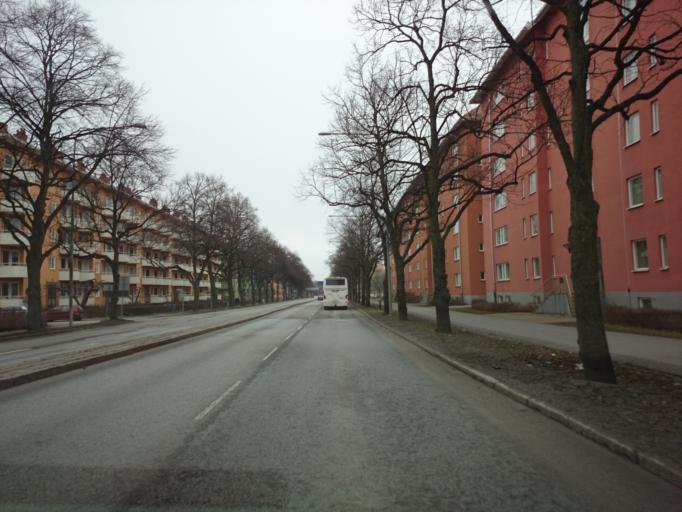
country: SE
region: Uppsala
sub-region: Uppsala Kommun
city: Uppsala
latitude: 59.8592
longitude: 17.6158
